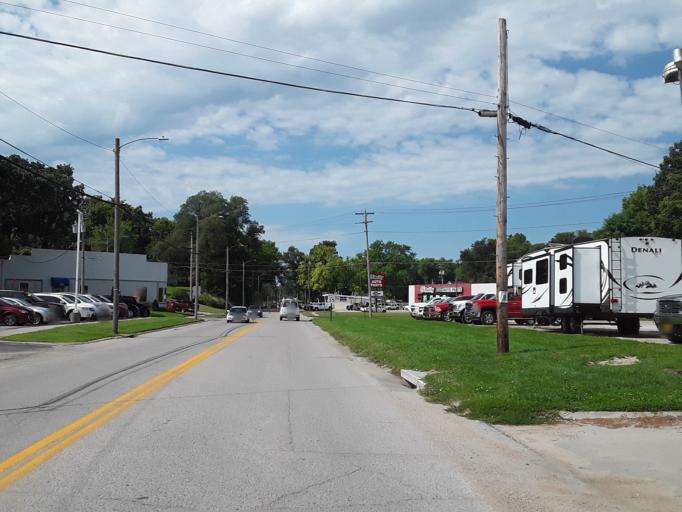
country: US
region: Nebraska
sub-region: Cass County
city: Plattsmouth
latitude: 41.0099
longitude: -95.8879
